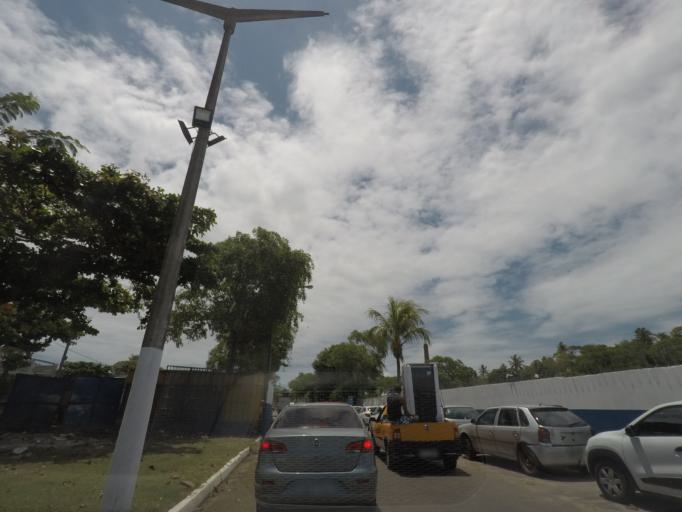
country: BR
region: Bahia
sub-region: Itaparica
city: Itaparica
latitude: -12.9270
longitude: -38.6209
